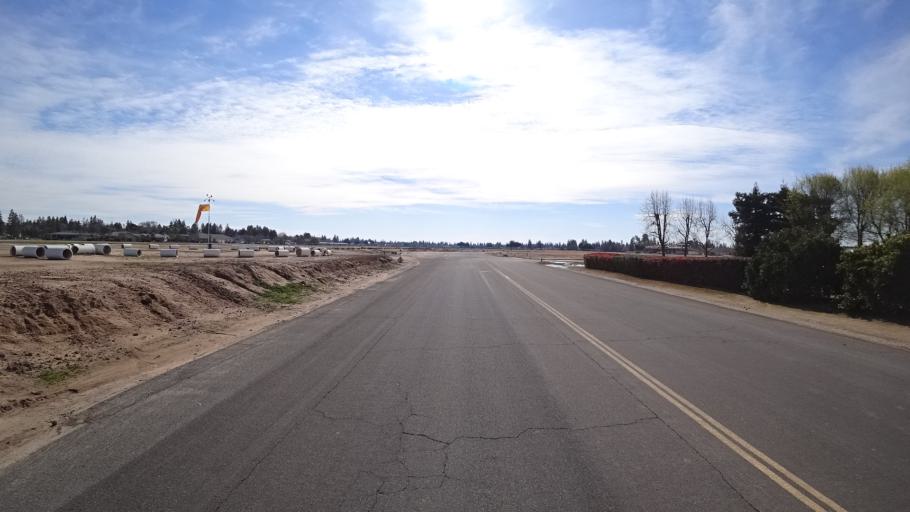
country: US
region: California
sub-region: Fresno County
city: West Park
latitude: 36.8398
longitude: -119.8707
